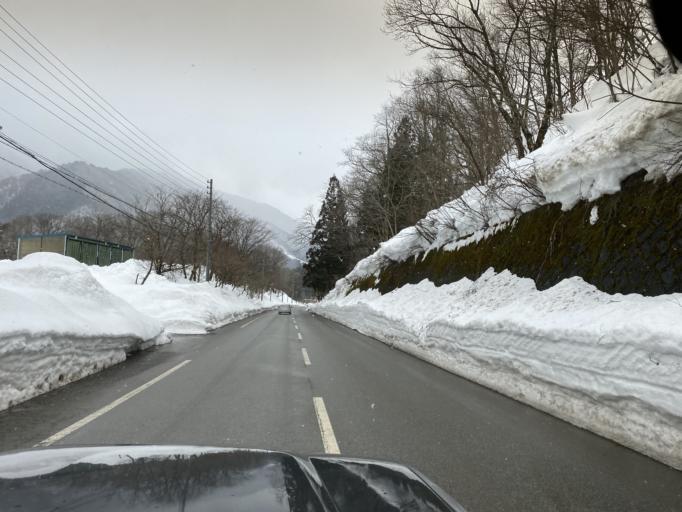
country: JP
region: Toyama
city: Fukumitsu
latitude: 36.2099
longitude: 136.8923
